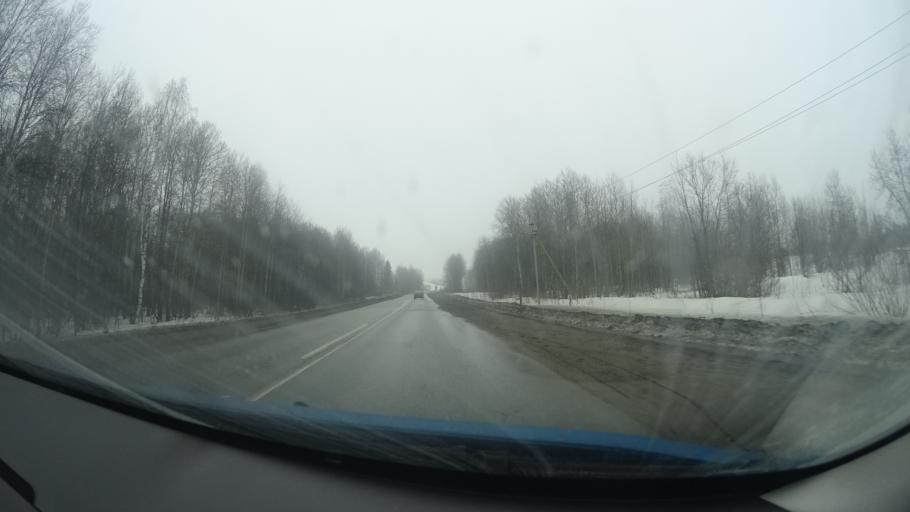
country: RU
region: Perm
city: Kuyeda
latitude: 56.4577
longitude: 55.6254
